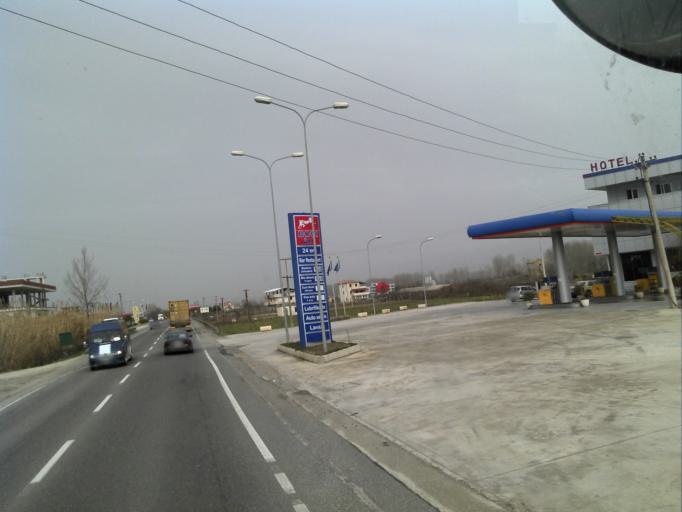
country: AL
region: Tirane
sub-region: Rrethi i Tiranes
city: Preze
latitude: 41.4420
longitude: 19.6885
